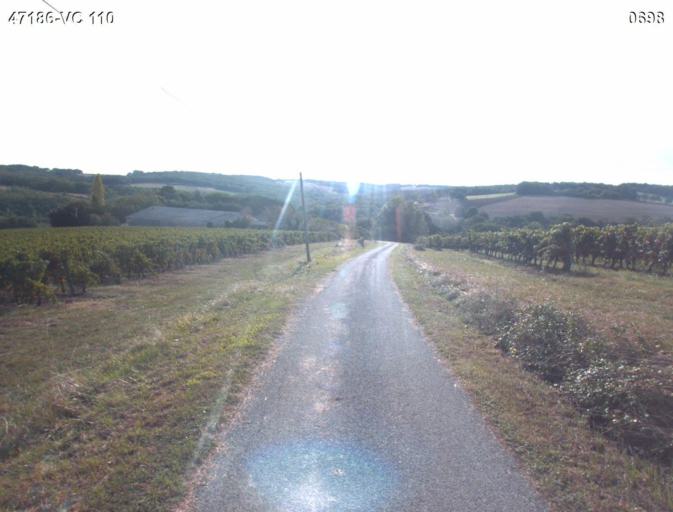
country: FR
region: Aquitaine
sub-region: Departement du Lot-et-Garonne
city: Port-Sainte-Marie
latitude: 44.1891
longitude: 0.4366
